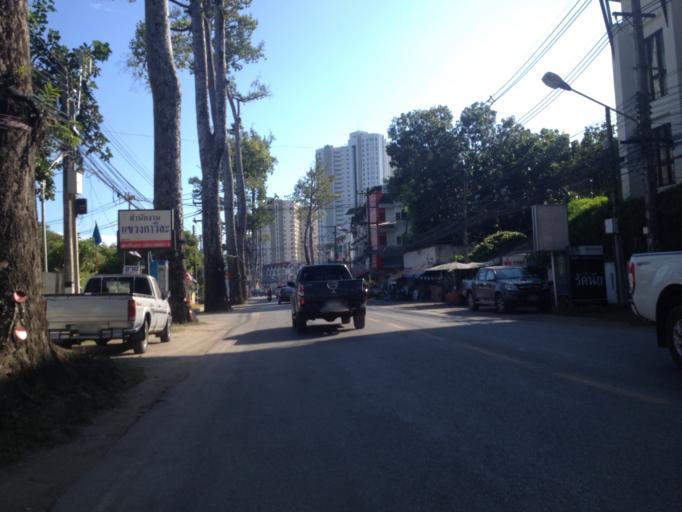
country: TH
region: Chiang Mai
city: Chiang Mai
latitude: 18.7695
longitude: 99.0062
